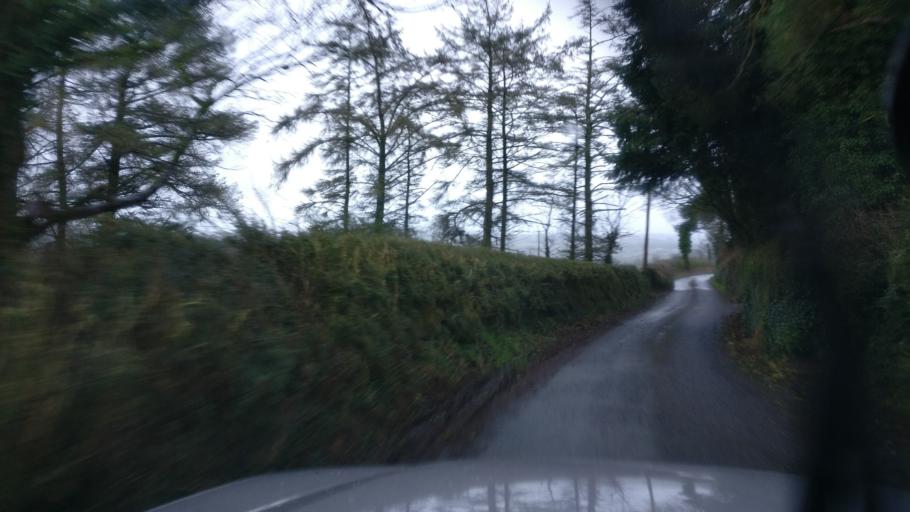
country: IE
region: Connaught
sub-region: County Galway
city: Loughrea
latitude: 53.1681
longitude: -8.6437
